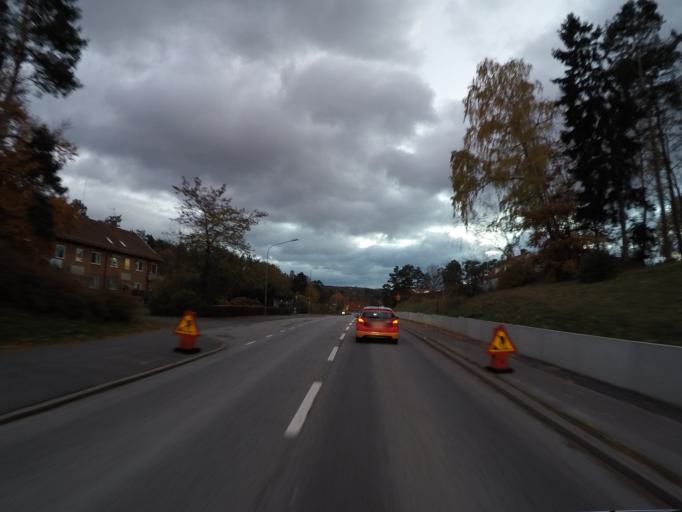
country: SE
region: Skane
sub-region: Kristianstads Kommun
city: Degeberga
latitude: 55.8333
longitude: 14.0902
